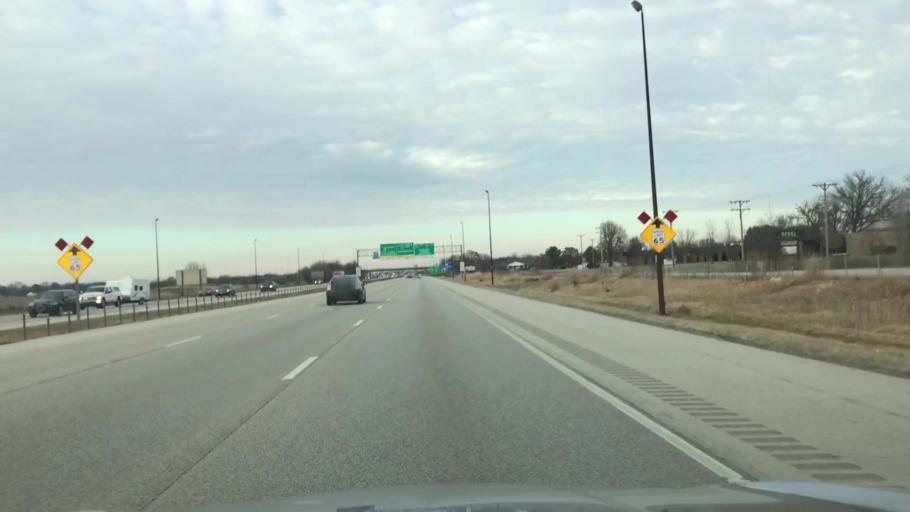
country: US
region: Illinois
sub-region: Sangamon County
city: Southern View
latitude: 39.7224
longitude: -89.6438
